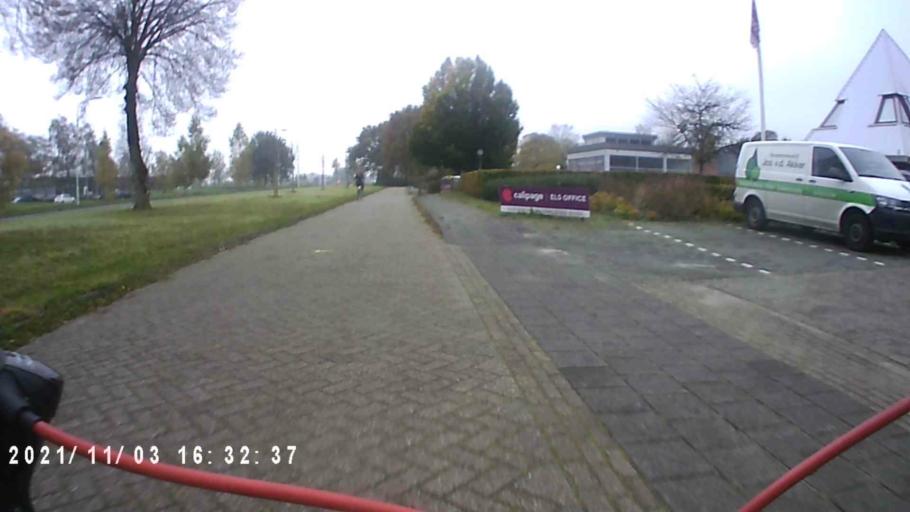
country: NL
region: Drenthe
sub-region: Gemeente Westerveld
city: Dwingeloo
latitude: 52.9796
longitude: 6.2936
